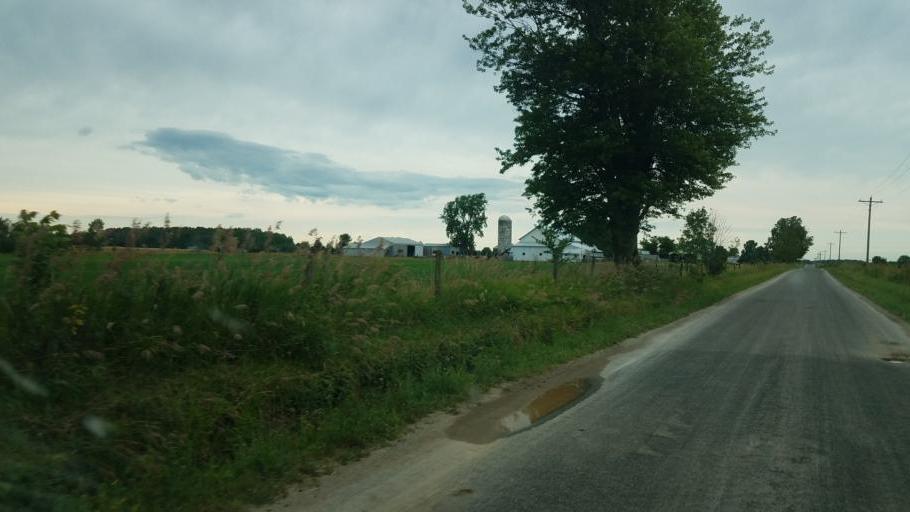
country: US
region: Ohio
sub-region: Ashland County
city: Ashland
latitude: 40.9398
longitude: -82.4073
